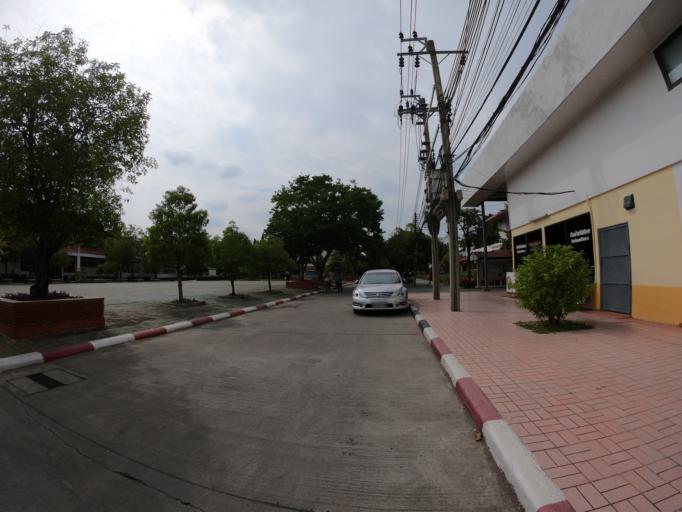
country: TH
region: Bangkok
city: Lat Phrao
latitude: 13.8262
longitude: 100.6163
